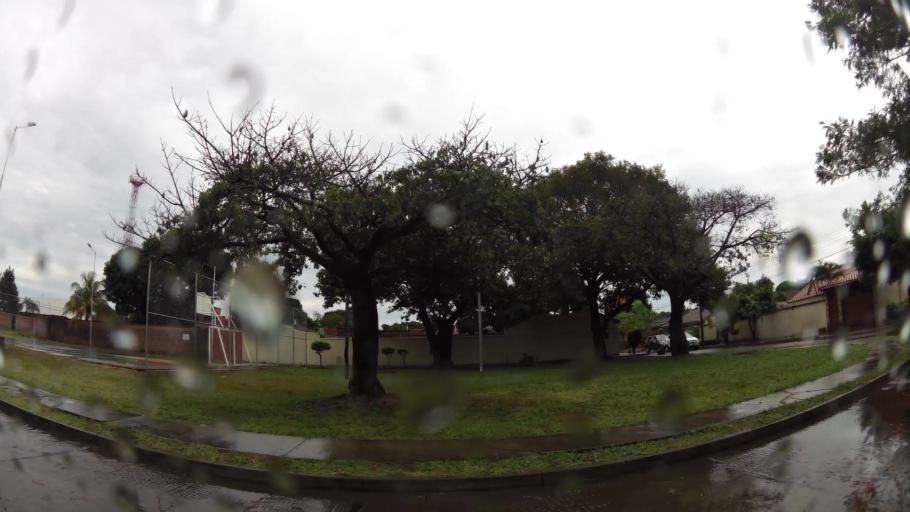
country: BO
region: Santa Cruz
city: Santa Cruz de la Sierra
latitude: -17.8081
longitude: -63.1654
